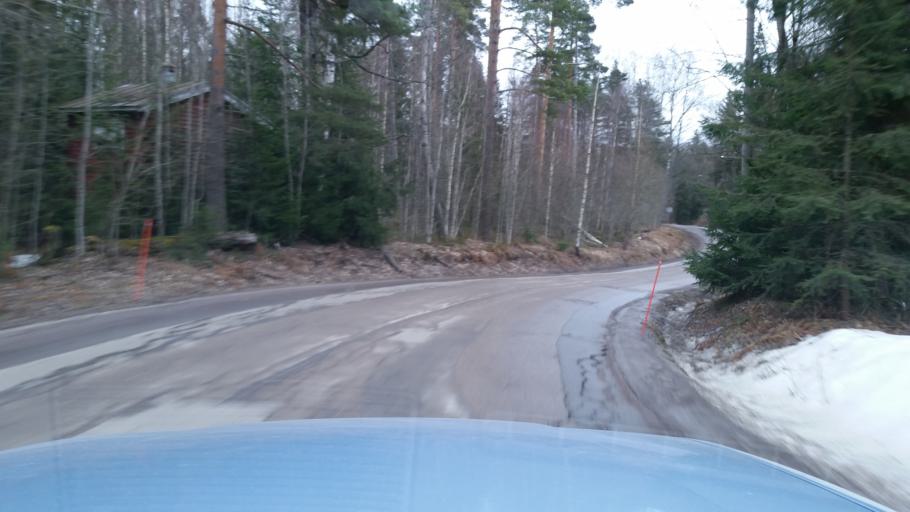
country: FI
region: Uusimaa
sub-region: Helsinki
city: Kauniainen
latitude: 60.2730
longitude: 24.6865
